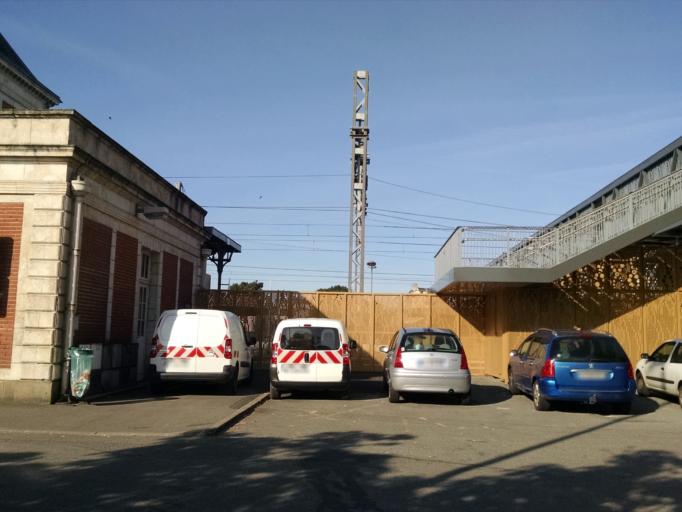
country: FR
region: Pays de la Loire
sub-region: Departement de la Loire-Atlantique
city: Clisson
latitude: 47.0863
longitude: -1.2864
